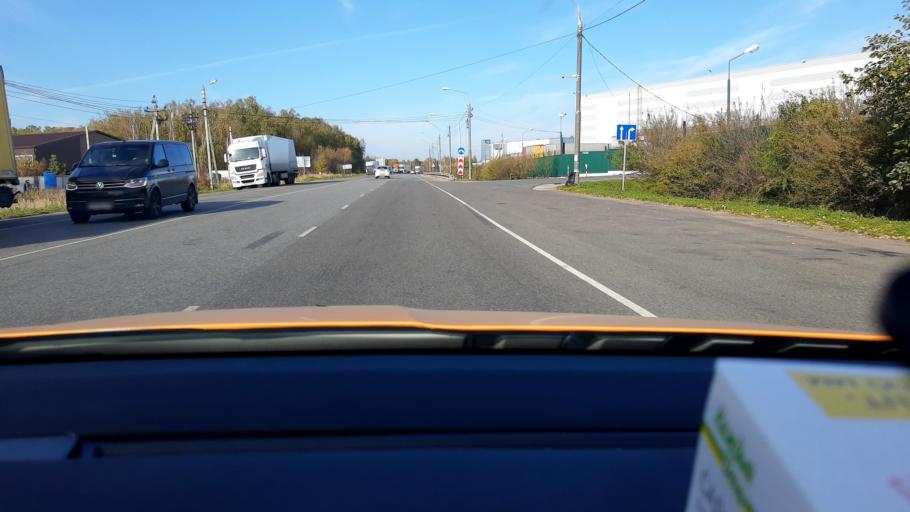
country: RU
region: Moskovskaya
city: Gorki-Leninskiye
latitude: 55.5117
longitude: 37.7866
